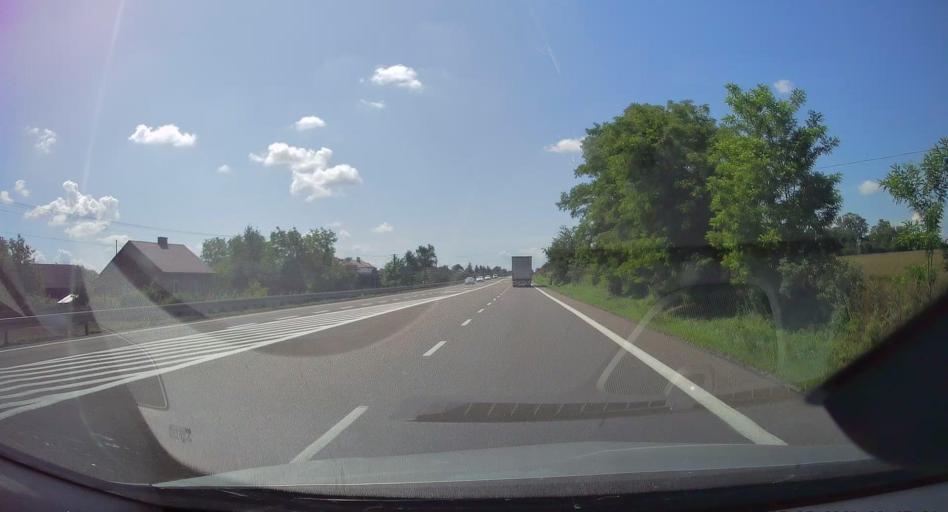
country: PL
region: Subcarpathian Voivodeship
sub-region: Powiat przemyski
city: Orly
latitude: 49.8982
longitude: 22.8164
